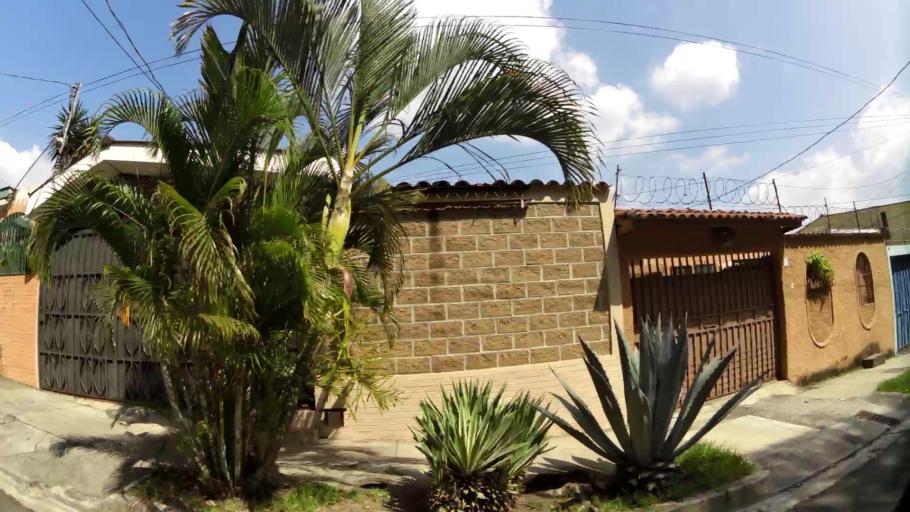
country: SV
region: San Salvador
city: Mejicanos
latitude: 13.7102
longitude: -89.2182
